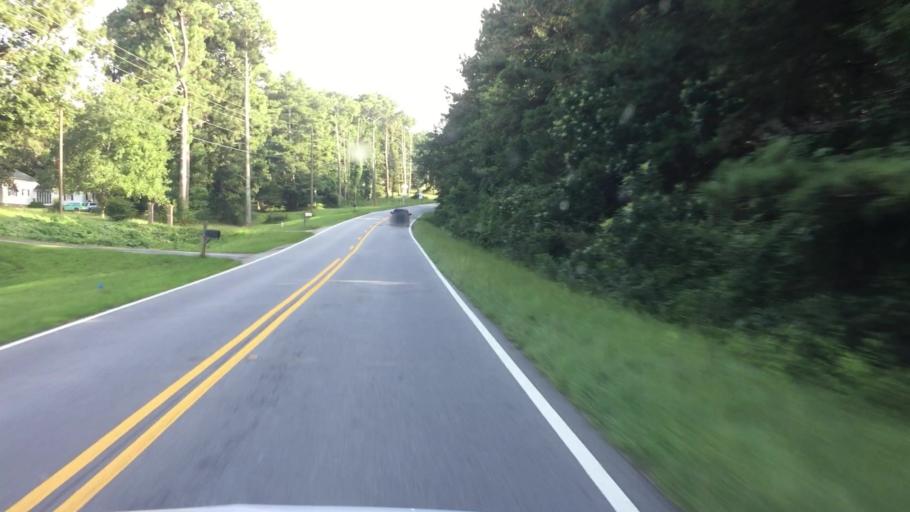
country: US
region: Georgia
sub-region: DeKalb County
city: Pine Mountain
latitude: 33.6236
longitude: -84.1305
